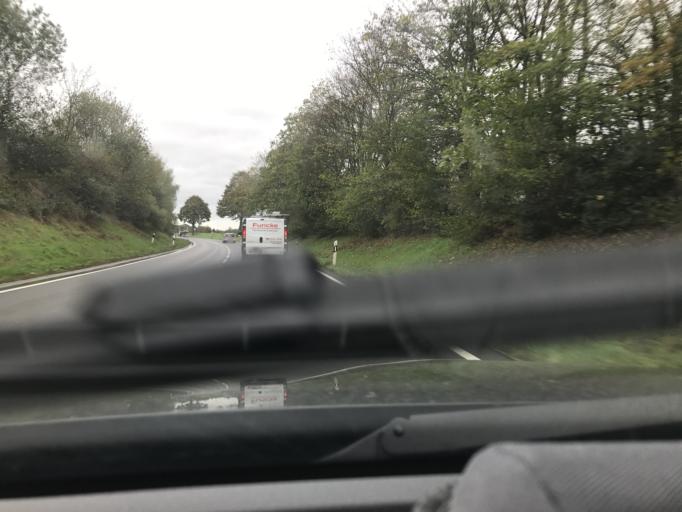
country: DE
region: North Rhine-Westphalia
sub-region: Regierungsbezirk Dusseldorf
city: Nettetal
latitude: 51.2918
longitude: 6.2889
